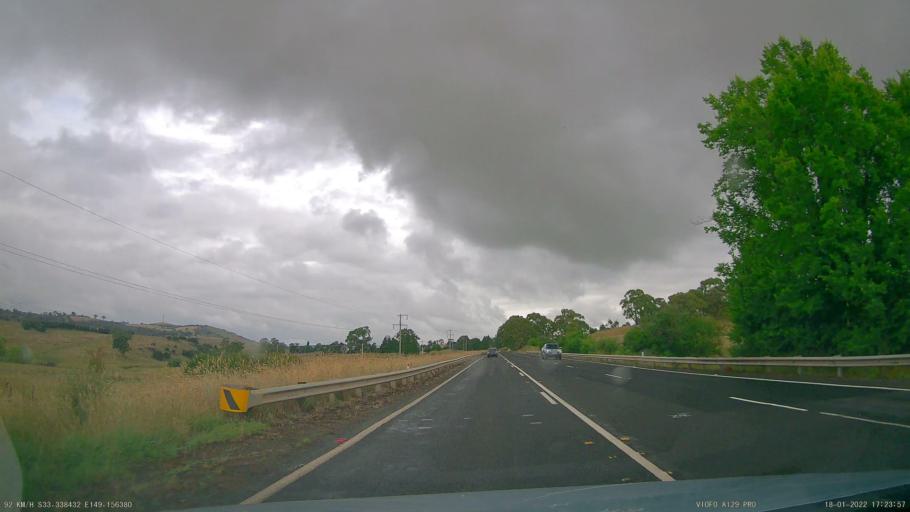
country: AU
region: New South Wales
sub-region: Orange Municipality
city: Orange
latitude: -33.3387
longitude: 149.1565
